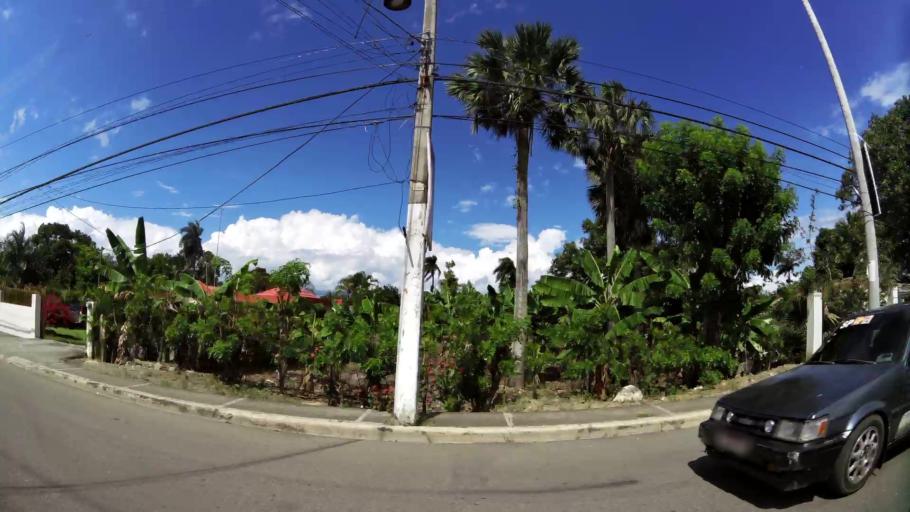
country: DO
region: Santiago
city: Licey al Medio
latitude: 19.3804
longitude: -70.6161
